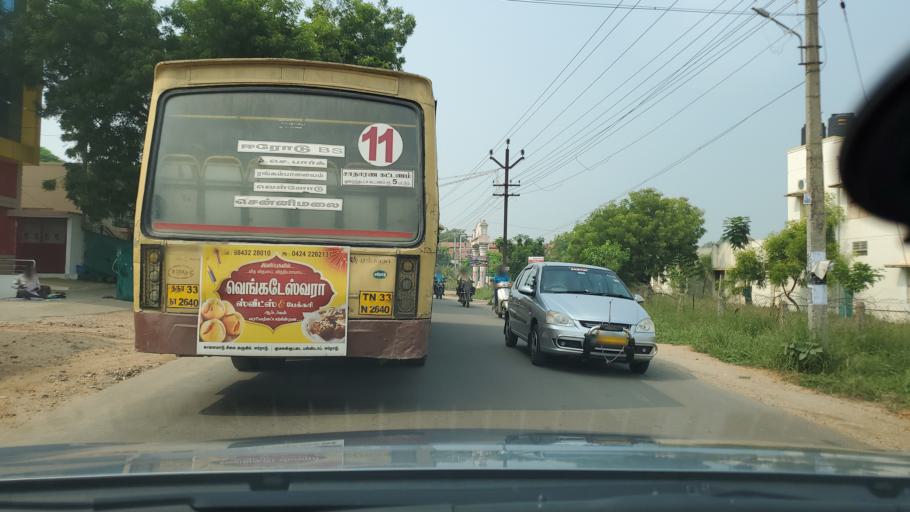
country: IN
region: Tamil Nadu
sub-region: Erode
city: Erode
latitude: 11.3142
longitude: 77.7103
